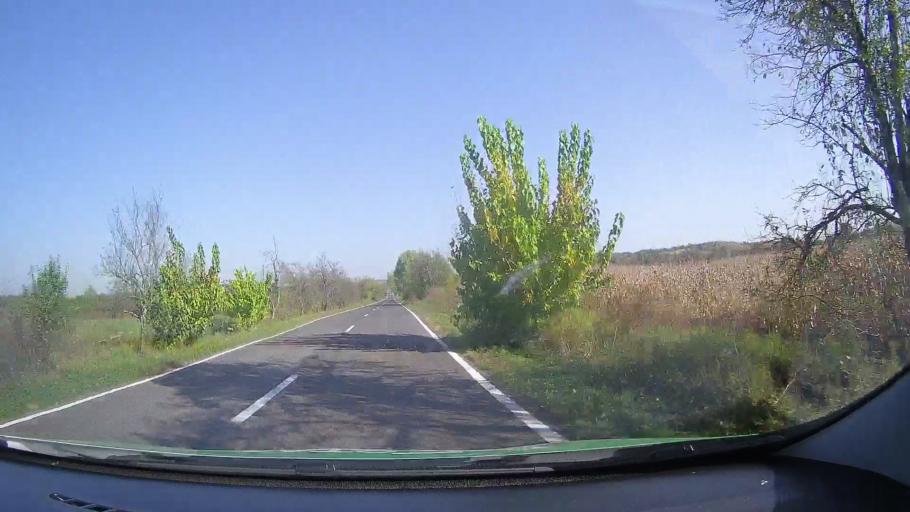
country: RO
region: Timis
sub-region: Comuna Curtea
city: Curtea
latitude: 45.8401
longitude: 22.3108
